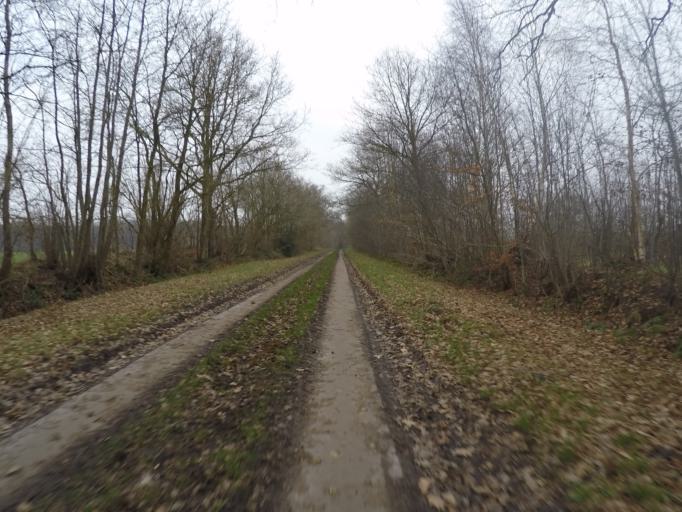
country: DE
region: Schleswig-Holstein
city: Borstel-Hohenraden
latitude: 53.7023
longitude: 9.8382
